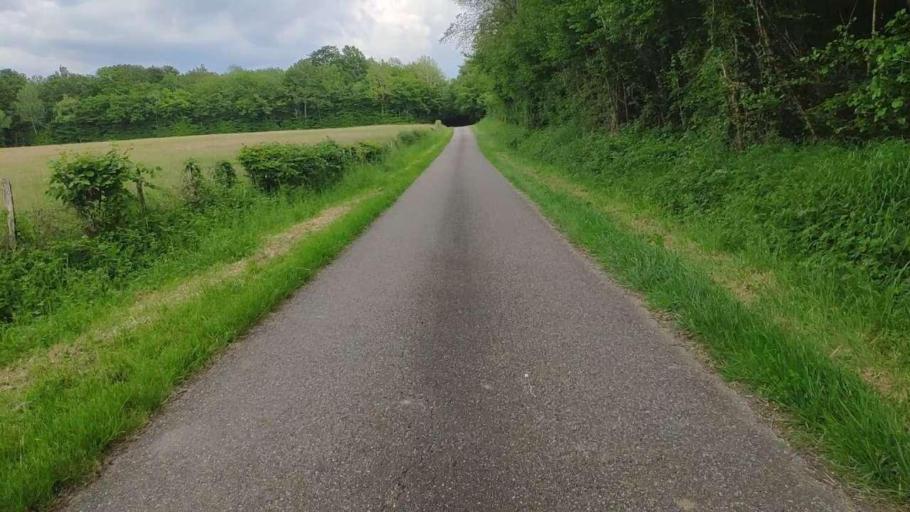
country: FR
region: Bourgogne
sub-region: Departement de Saone-et-Loire
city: Saint-Germain-du-Bois
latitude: 46.7966
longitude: 5.3499
